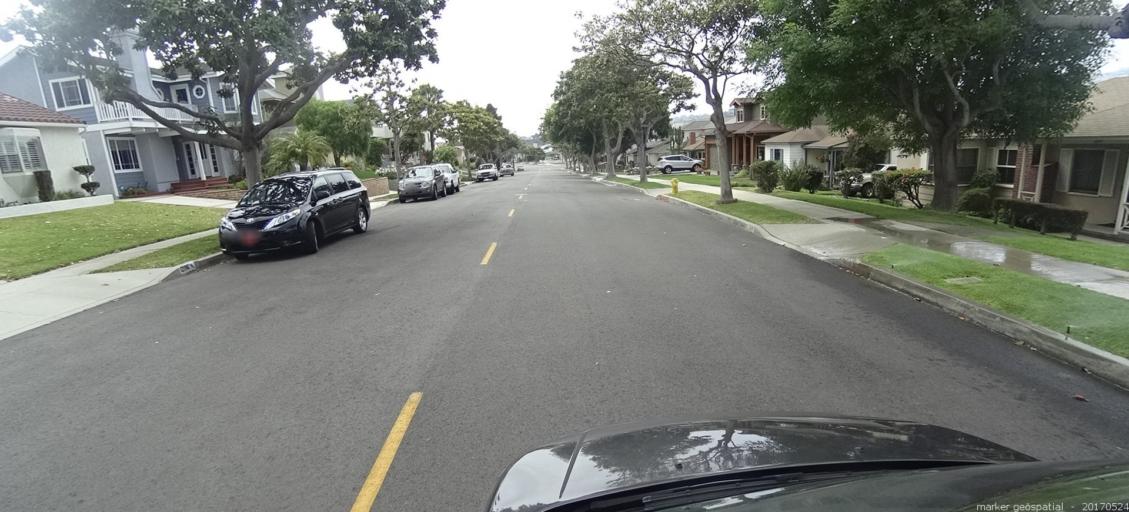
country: US
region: California
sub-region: Los Angeles County
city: Palos Verdes Estates
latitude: 33.8235
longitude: -118.3802
